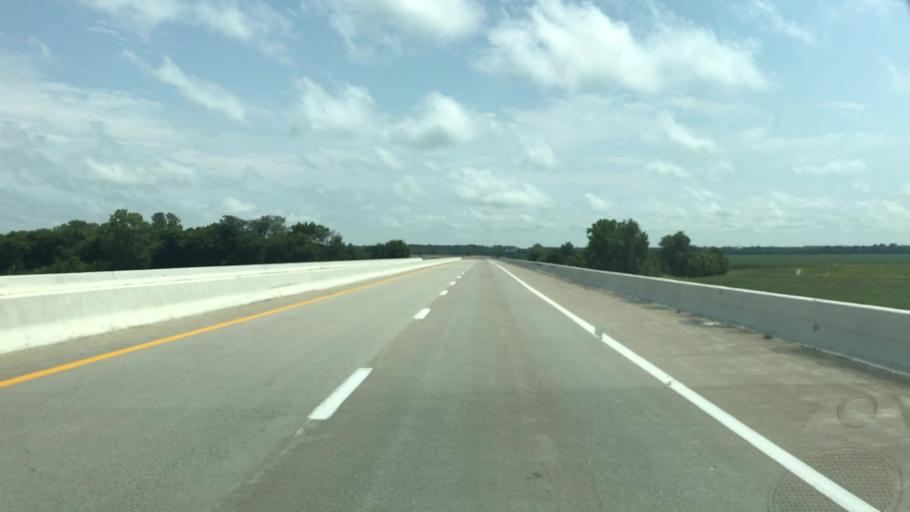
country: US
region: Missouri
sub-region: Pemiscot County
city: Caruthersville
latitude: 36.1052
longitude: -89.6075
